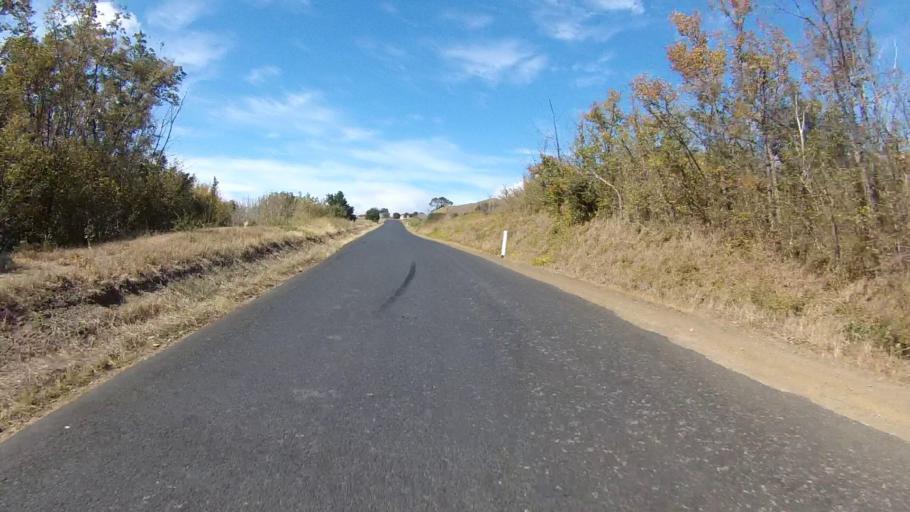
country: AU
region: Tasmania
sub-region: Brighton
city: Bridgewater
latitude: -42.7331
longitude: 147.2604
